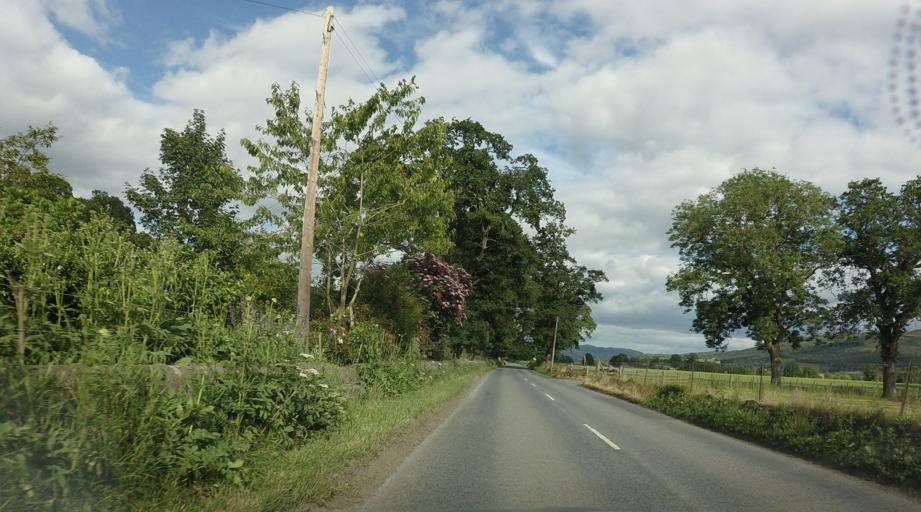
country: GB
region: Scotland
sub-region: Perth and Kinross
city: Pitlochry
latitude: 56.6595
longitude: -3.7442
